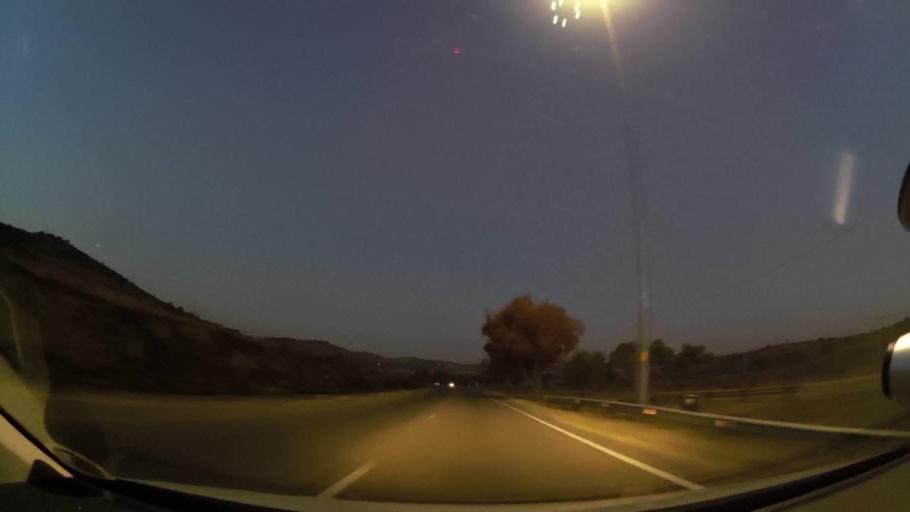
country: ZA
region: Gauteng
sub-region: City of Tshwane Metropolitan Municipality
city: Pretoria
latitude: -25.7825
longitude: 28.1778
